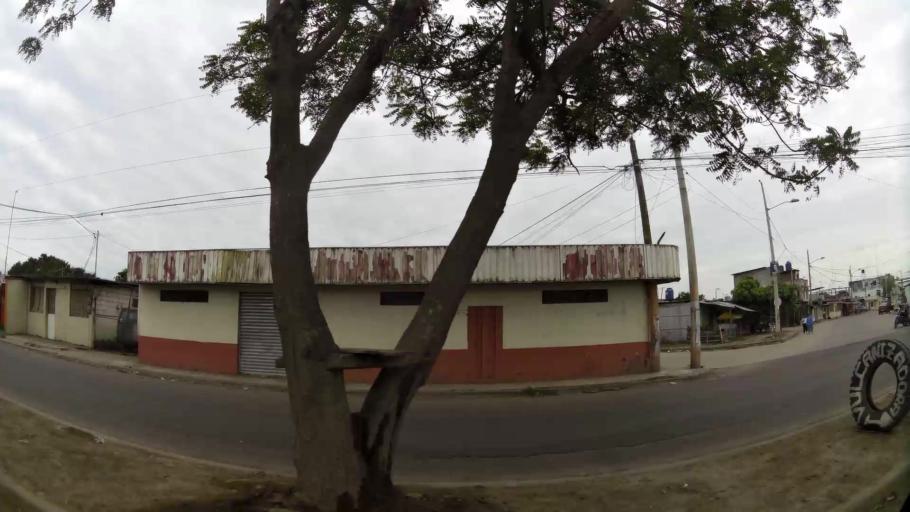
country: EC
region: El Oro
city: Machala
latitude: -3.2458
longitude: -79.9539
